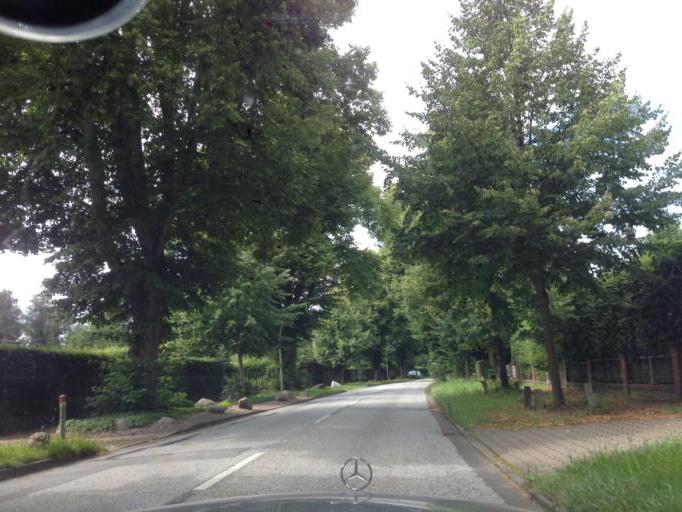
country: DE
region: Hamburg
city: Wohldorf-Ohlstedt
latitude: 53.6994
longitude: 10.1236
